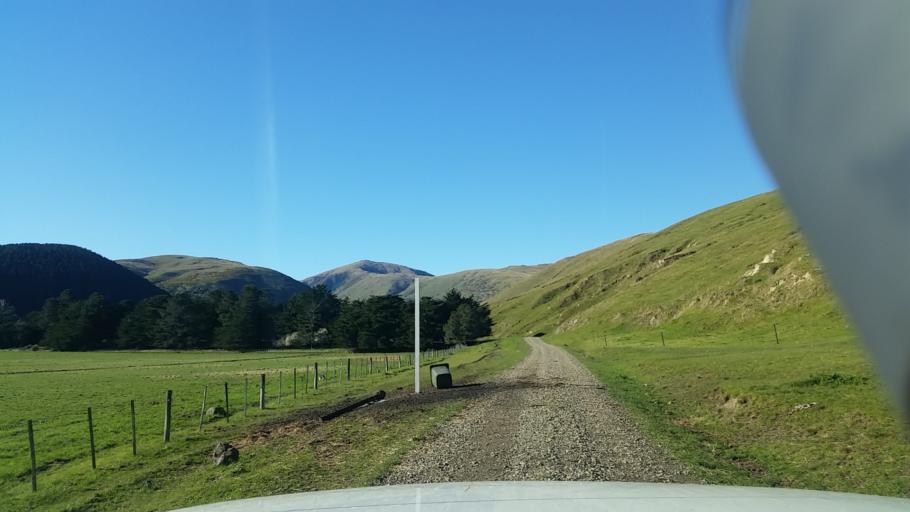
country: NZ
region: Canterbury
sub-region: Selwyn District
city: Lincoln
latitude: -43.7997
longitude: 172.6895
